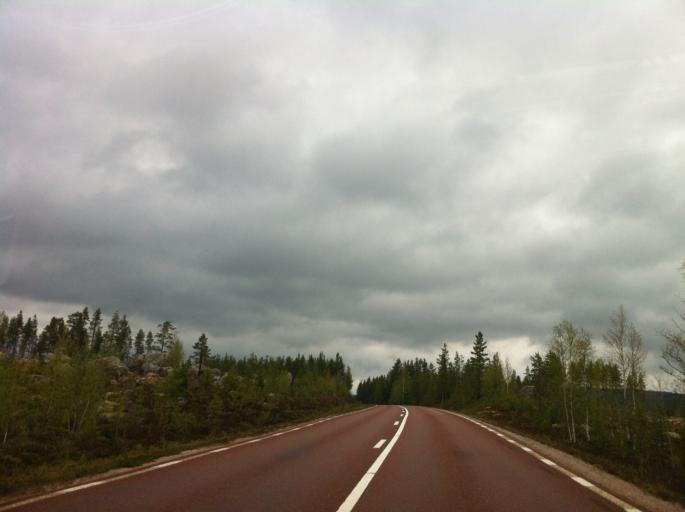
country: SE
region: Jaemtland
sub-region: Harjedalens Kommun
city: Sveg
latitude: 61.9068
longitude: 14.6214
